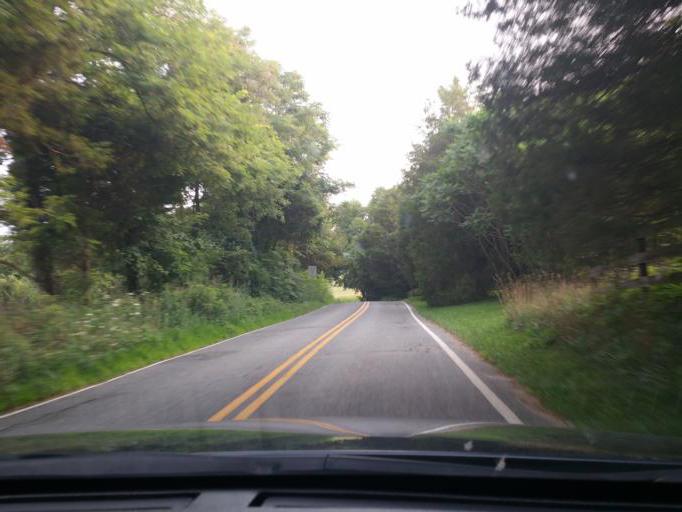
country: US
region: Maryland
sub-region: Cecil County
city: Rising Sun
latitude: 39.7198
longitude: -76.2006
